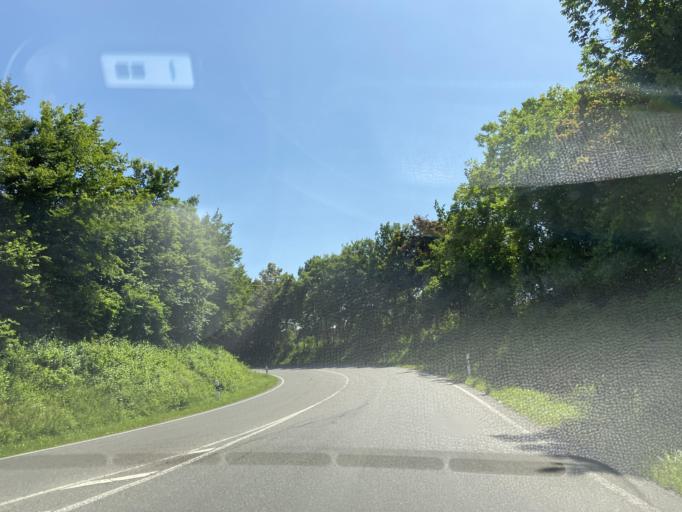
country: DE
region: Baden-Wuerttemberg
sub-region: Tuebingen Region
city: Balingen
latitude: 48.2568
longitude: 8.8538
